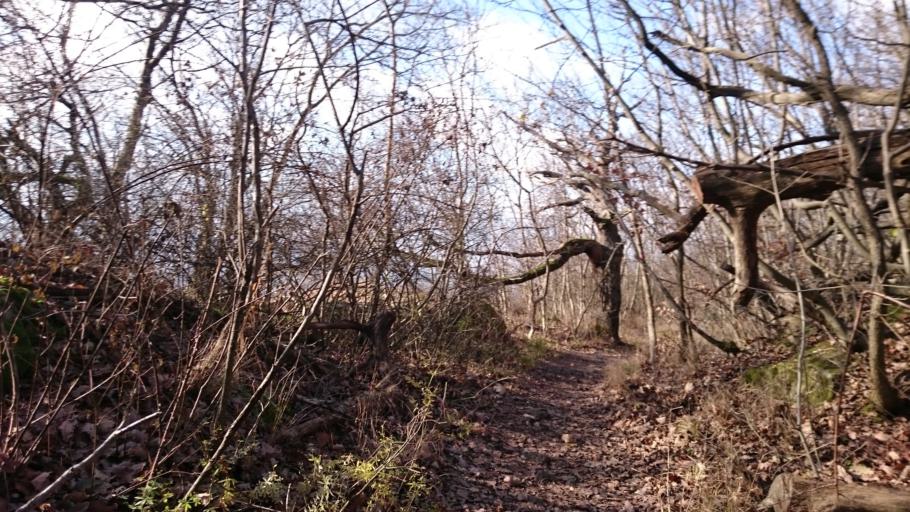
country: HU
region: Pest
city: Pilisborosjeno
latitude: 47.6140
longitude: 18.9992
